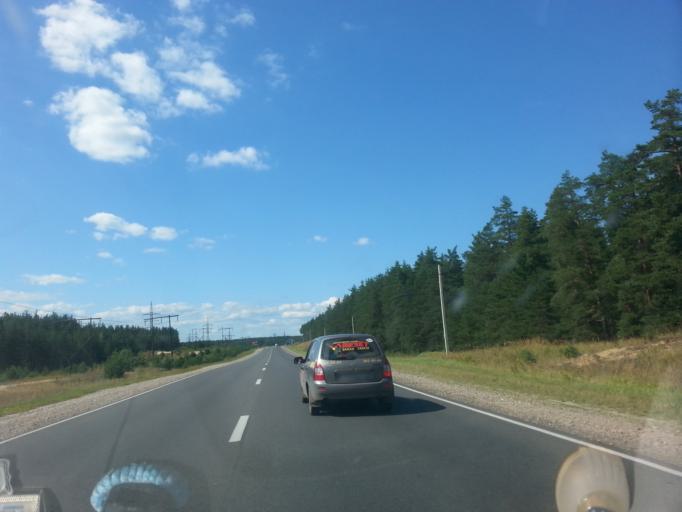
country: RU
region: Nizjnij Novgorod
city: Lukino
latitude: 56.3992
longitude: 43.6654
